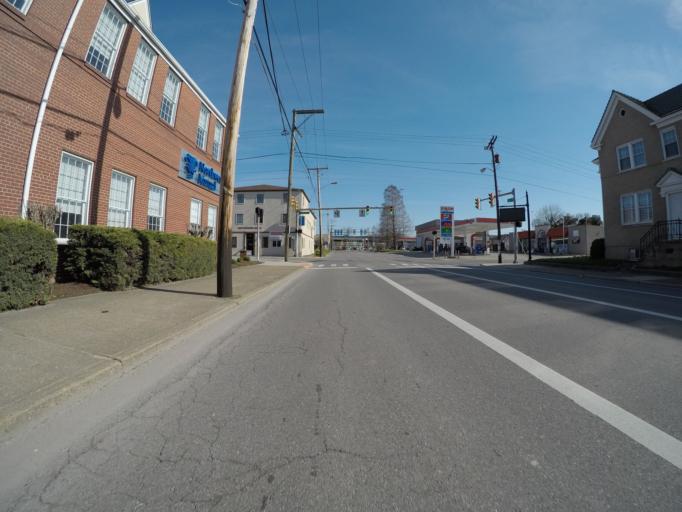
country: US
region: West Virginia
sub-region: Kanawha County
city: Charleston
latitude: 38.3606
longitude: -81.6426
